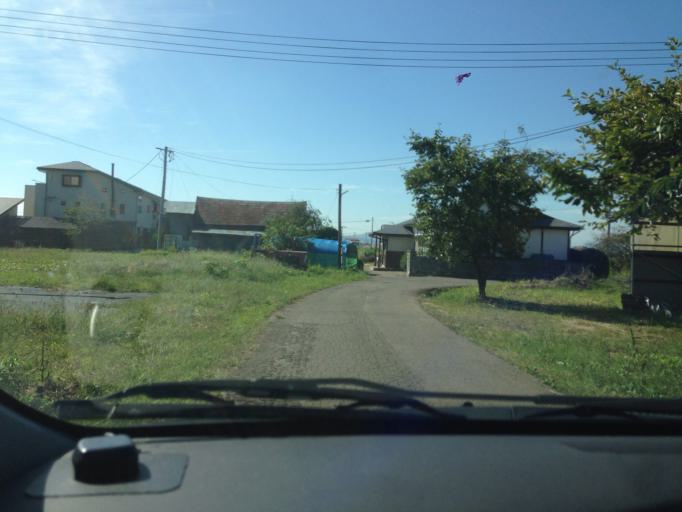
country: JP
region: Fukushima
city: Kitakata
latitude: 37.5499
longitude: 139.9163
